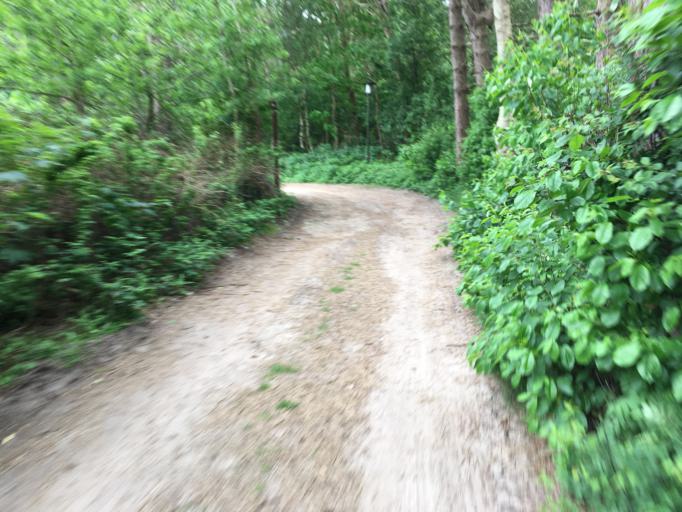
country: DE
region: Schleswig-Holstein
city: Norddorf
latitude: 54.6737
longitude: 8.3313
